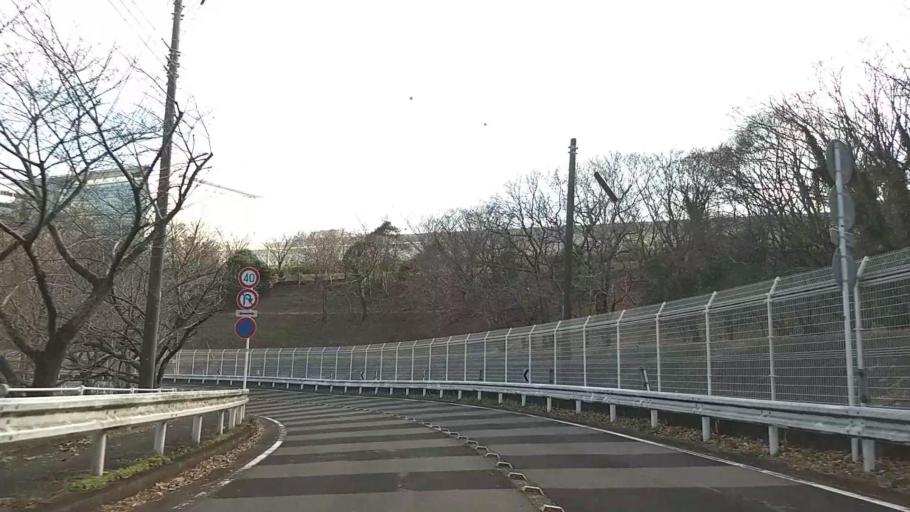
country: JP
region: Kanagawa
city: Isehara
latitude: 35.4254
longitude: 139.3145
